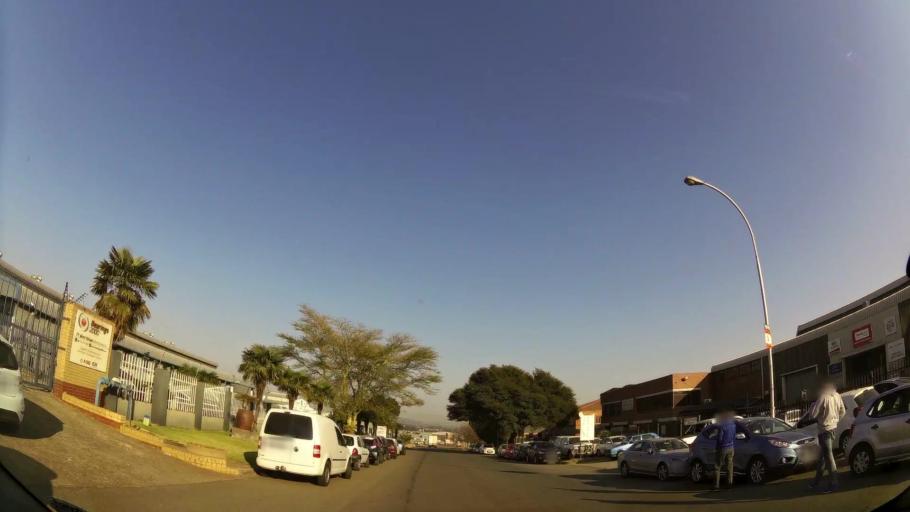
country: ZA
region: Gauteng
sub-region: City of Johannesburg Metropolitan Municipality
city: Modderfontein
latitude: -26.1475
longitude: 28.1859
